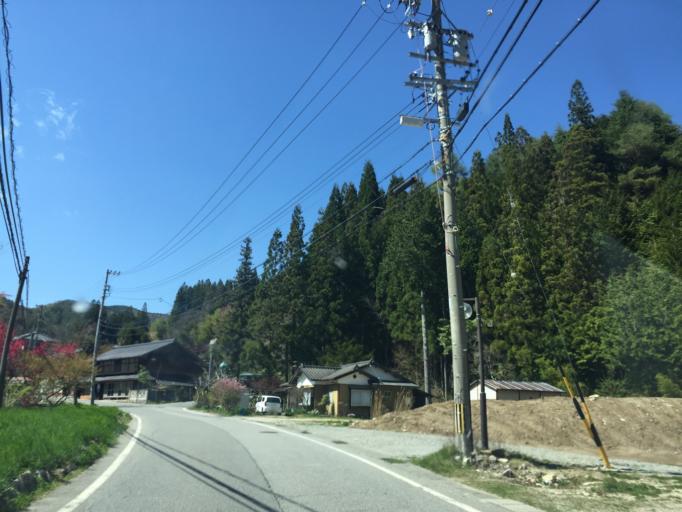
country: JP
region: Nagano
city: Iida
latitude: 35.3836
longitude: 137.6867
